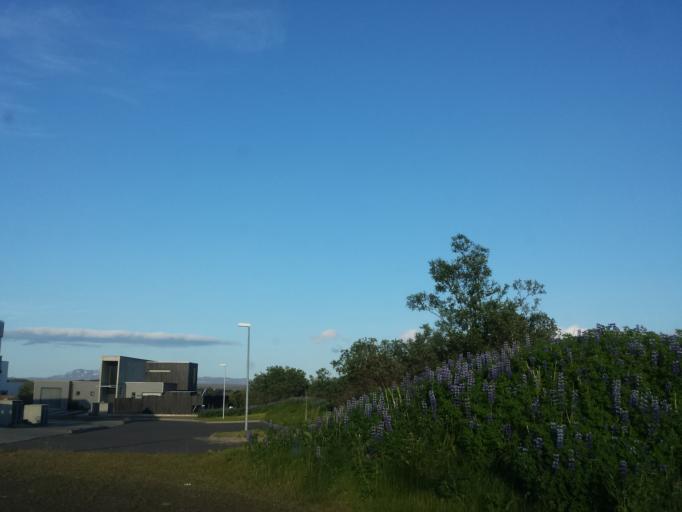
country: IS
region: Capital Region
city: Mosfellsbaer
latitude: 64.0954
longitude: -21.7785
